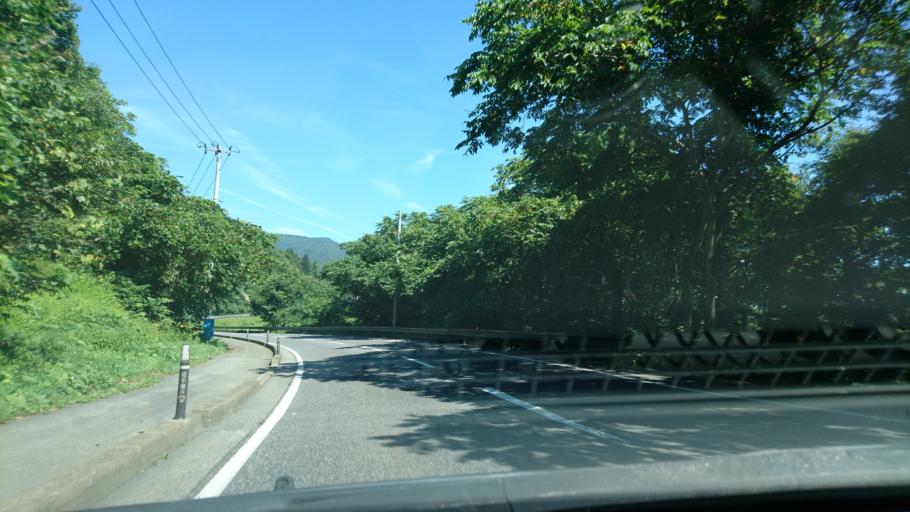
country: JP
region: Iwate
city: Tono
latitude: 39.3351
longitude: 141.5193
